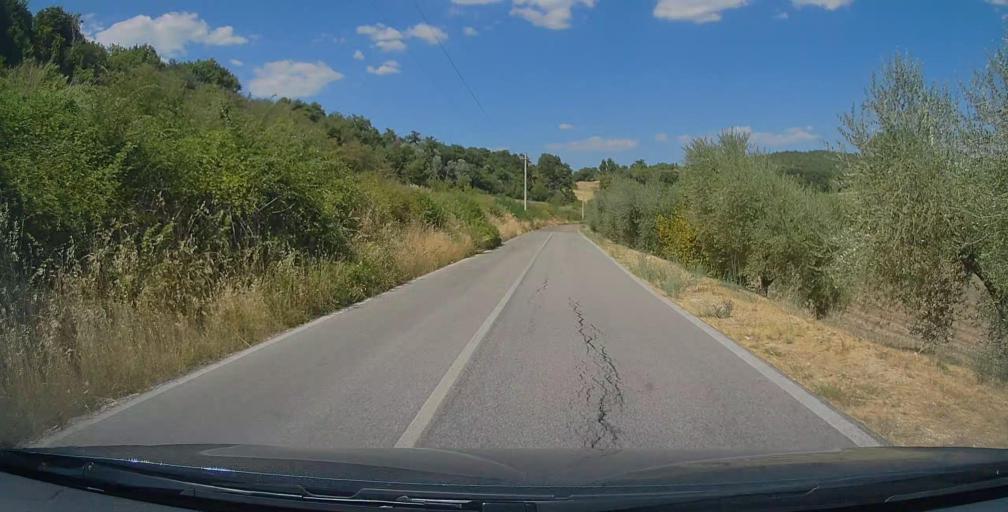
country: IT
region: Umbria
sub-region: Provincia di Terni
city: Otricoli
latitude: 42.3952
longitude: 12.4686
